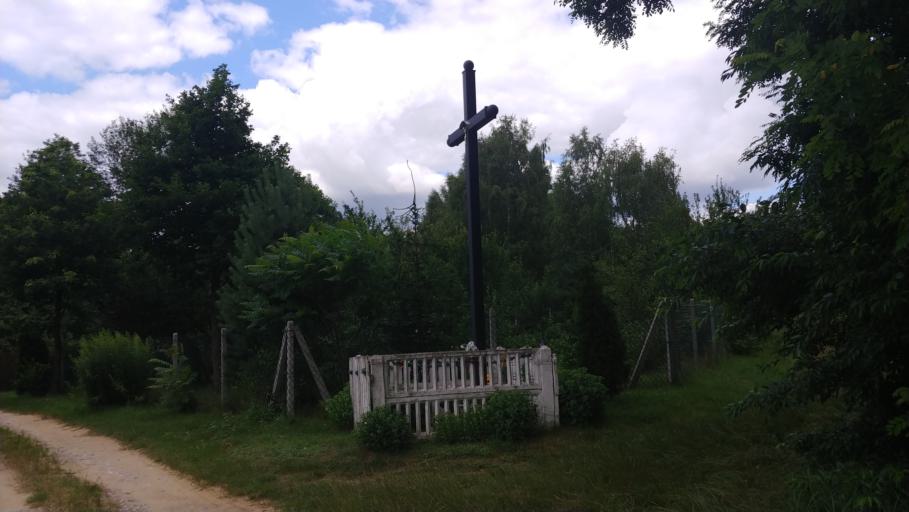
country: PL
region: Lodz Voivodeship
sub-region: Powiat skierniewicki
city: Gluchow
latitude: 51.7493
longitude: 20.0584
